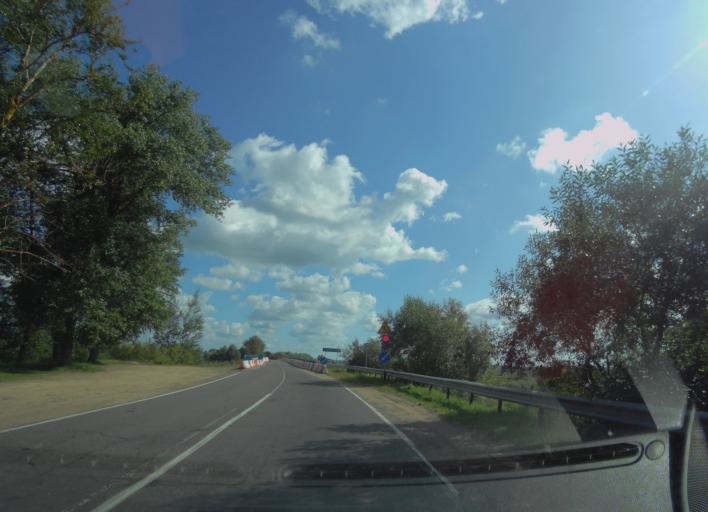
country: BY
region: Minsk
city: Zyembin
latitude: 54.3579
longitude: 28.3326
